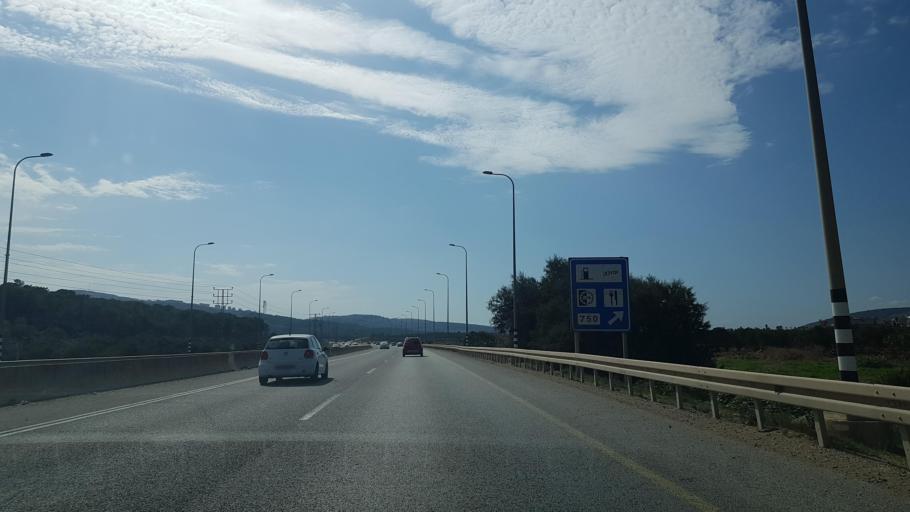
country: IL
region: Northern District
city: Bu`eina
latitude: 32.7692
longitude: 35.3856
